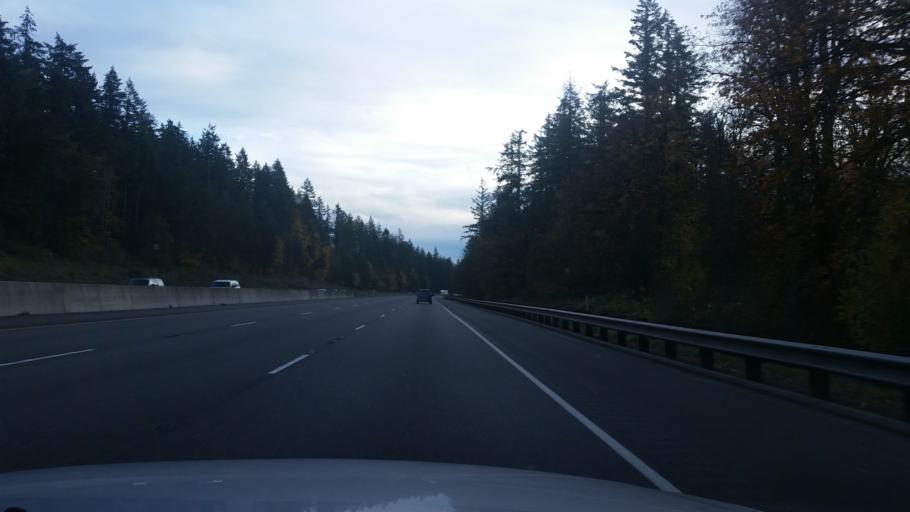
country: US
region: Washington
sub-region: Thurston County
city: Grand Mound
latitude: 46.8633
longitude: -122.9718
